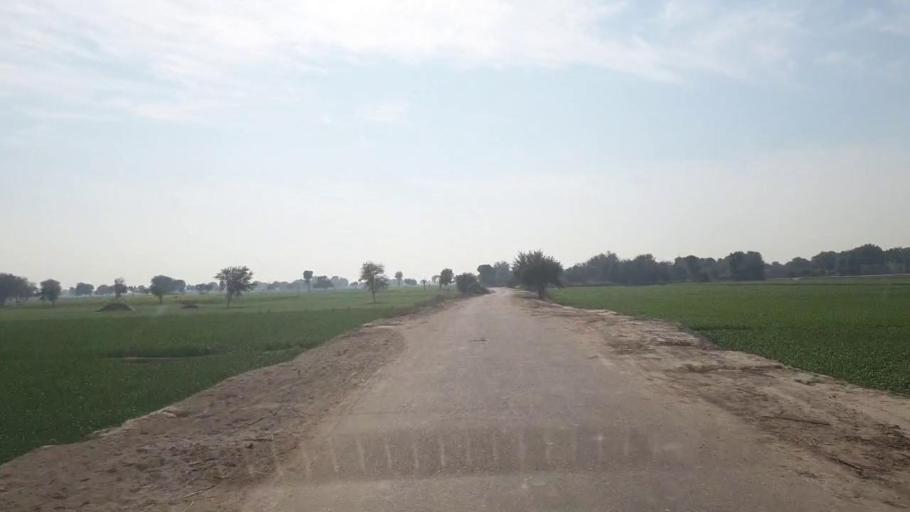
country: PK
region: Sindh
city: Shahpur Chakar
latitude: 26.1539
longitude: 68.5151
